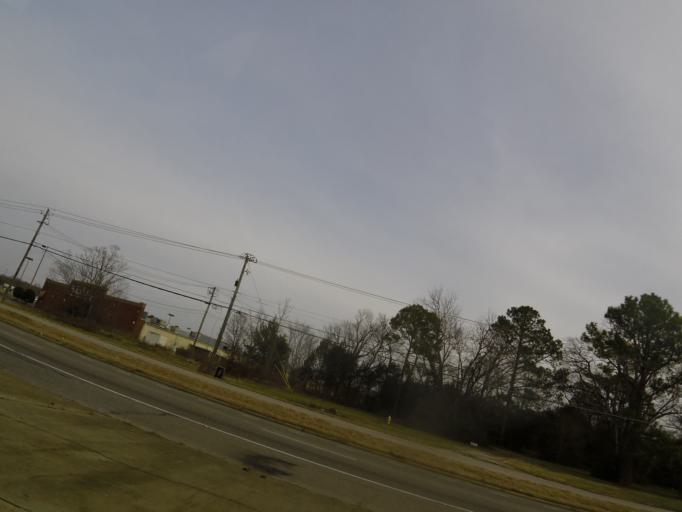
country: US
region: Alabama
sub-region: Montgomery County
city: Montgomery
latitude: 32.3244
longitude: -86.2394
